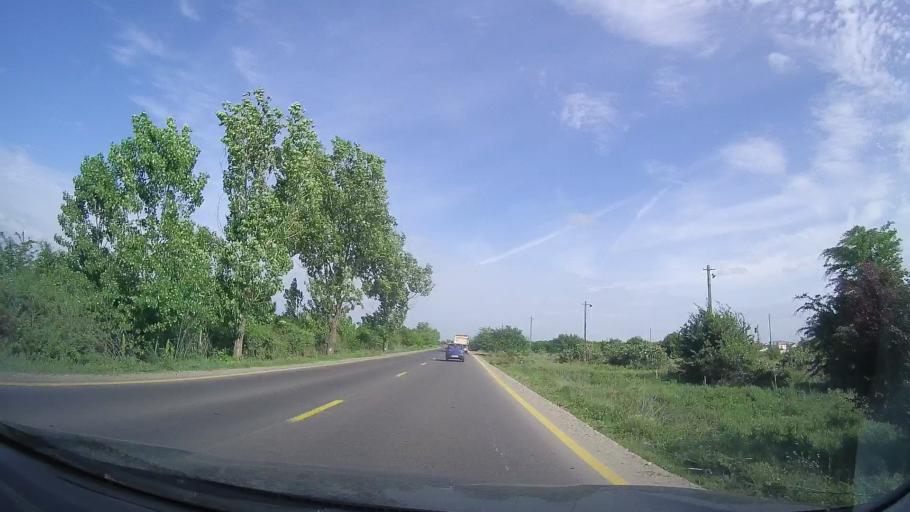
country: RO
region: Ilfov
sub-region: Comuna Magurele
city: Varteju
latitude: 44.3733
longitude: 26.0081
